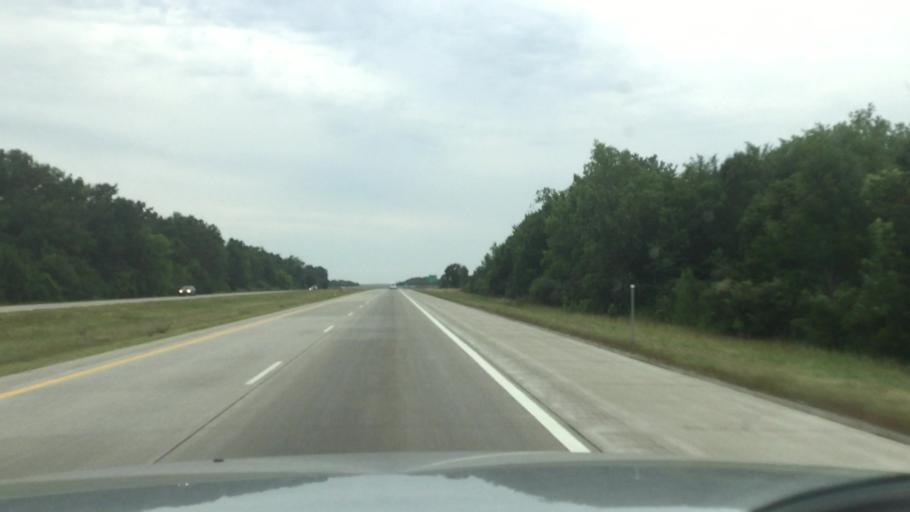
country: US
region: Michigan
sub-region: Genesee County
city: Grand Blanc
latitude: 42.9348
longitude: -83.6811
